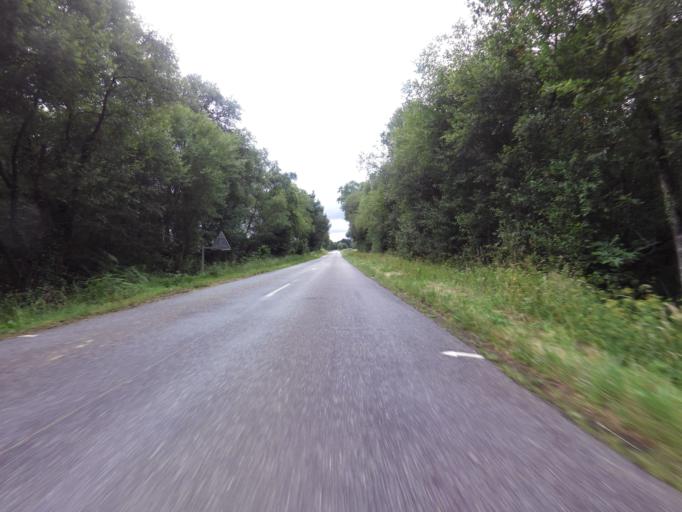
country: FR
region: Brittany
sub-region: Departement du Morbihan
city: Malansac
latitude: 47.7263
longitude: -2.3022
